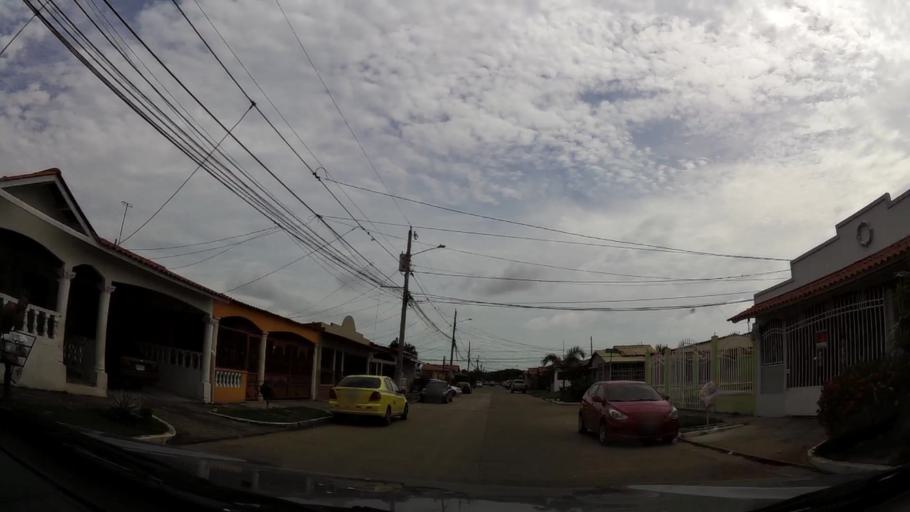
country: PA
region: Panama
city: Tocumen
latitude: 9.0432
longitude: -79.4107
